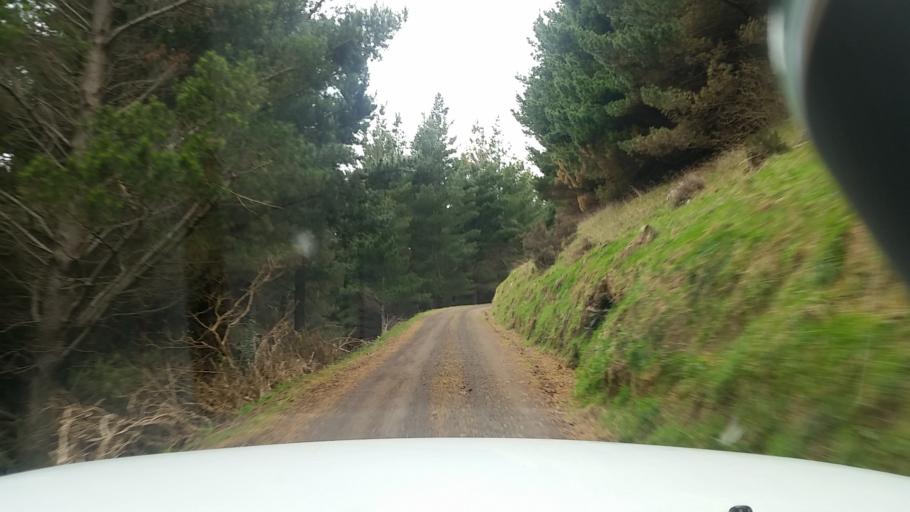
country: NZ
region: Canterbury
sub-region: Christchurch City
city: Christchurch
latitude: -43.7079
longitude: 172.7795
